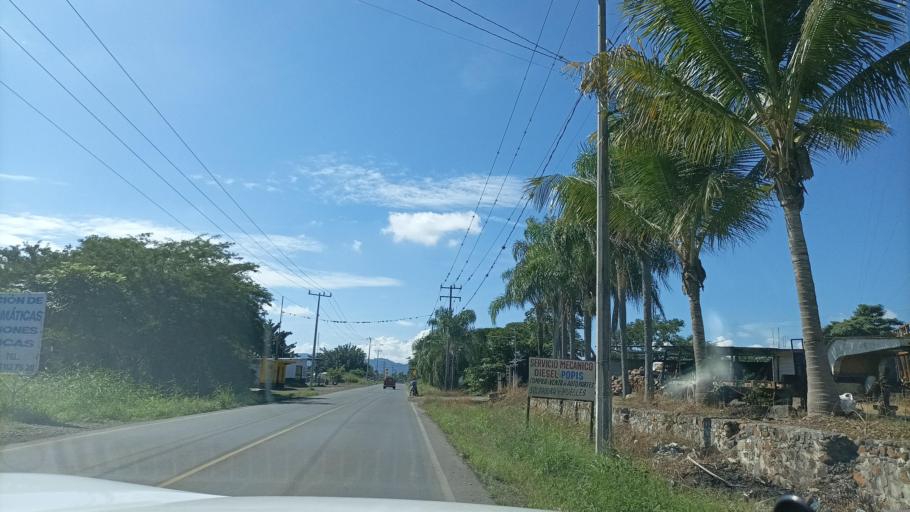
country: MX
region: Veracruz
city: Paso del Macho
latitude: 18.9688
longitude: -96.7327
